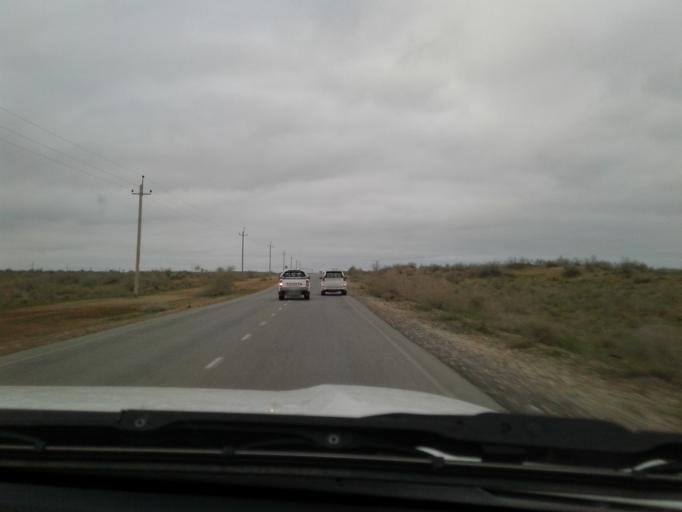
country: TM
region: Lebap
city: Farap
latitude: 39.0977
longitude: 63.7187
